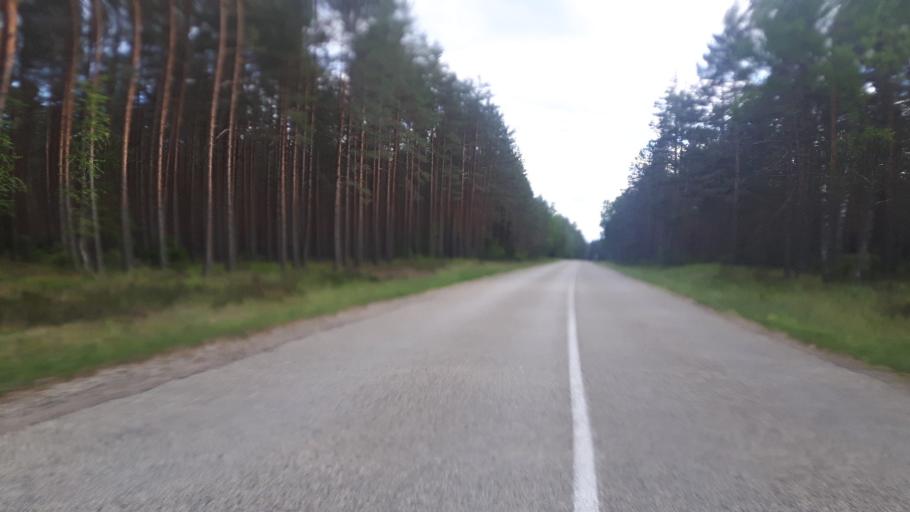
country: LV
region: Engure
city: Smarde
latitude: 57.0196
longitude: 23.3451
